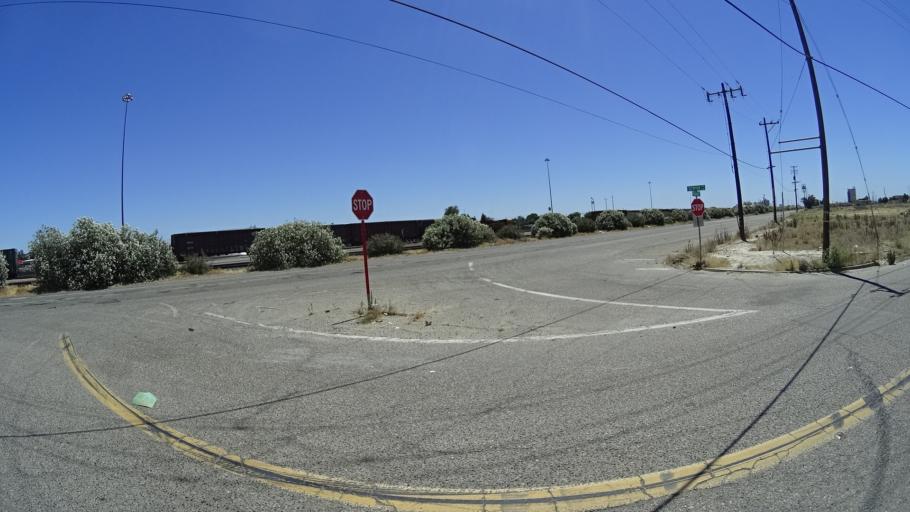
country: US
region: California
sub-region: Fresno County
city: Fresno
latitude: 36.7045
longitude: -119.7638
